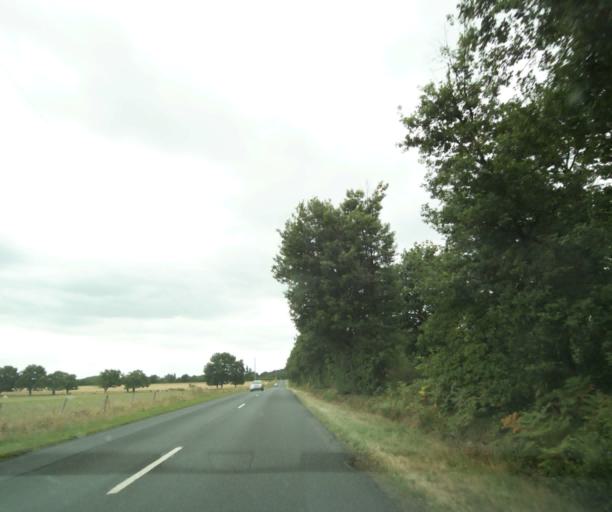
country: FR
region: Pays de la Loire
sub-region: Departement de la Sarthe
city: Precigne
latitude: 47.7975
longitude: -0.3209
